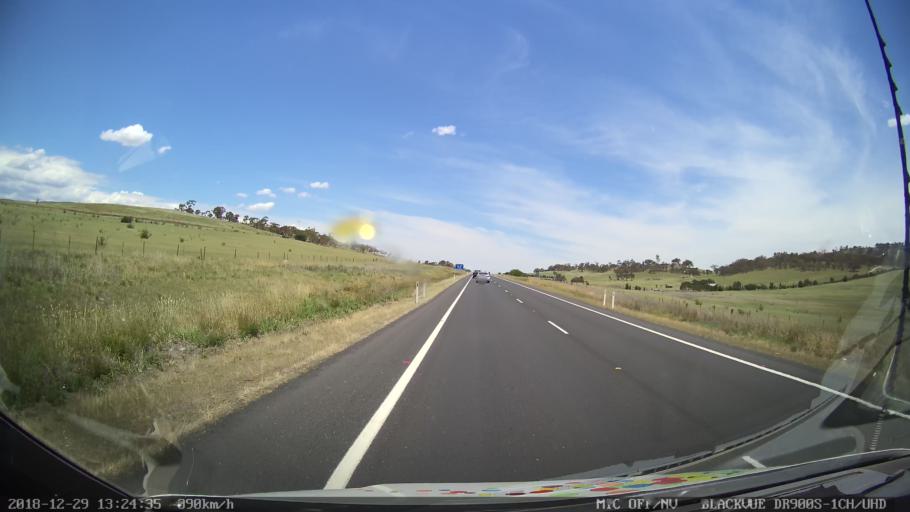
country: AU
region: New South Wales
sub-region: Cooma-Monaro
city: Cooma
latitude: -35.8316
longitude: 149.1624
